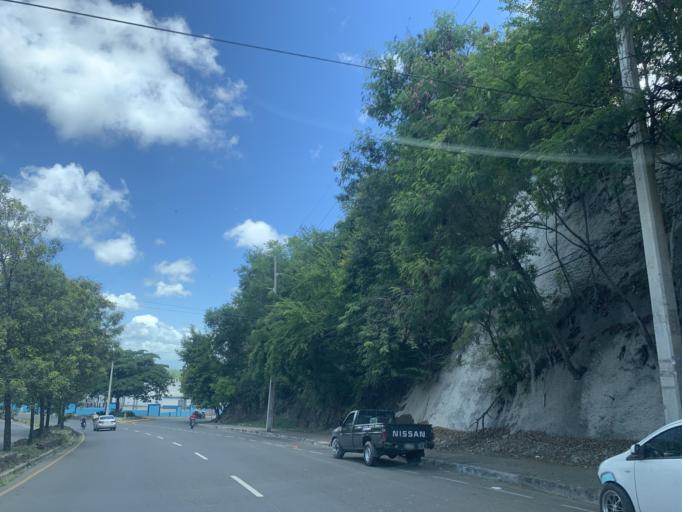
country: DO
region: Nacional
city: La Agustina
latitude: 18.5071
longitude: -69.9176
